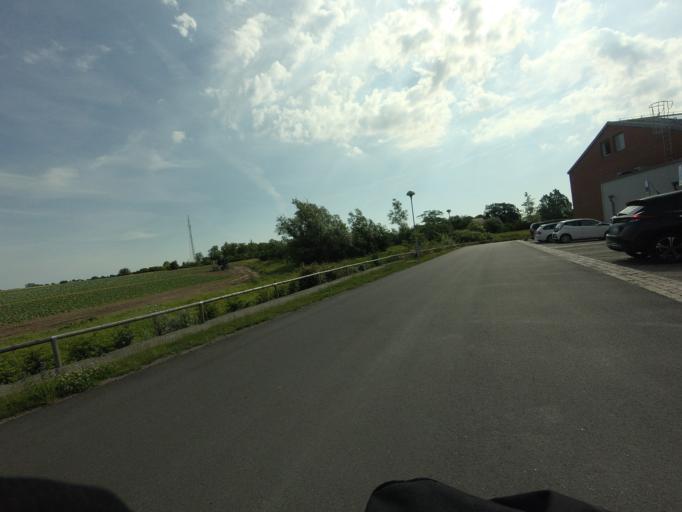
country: SE
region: Skane
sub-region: Malmo
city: Tygelsjo
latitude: 55.4991
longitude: 13.0059
